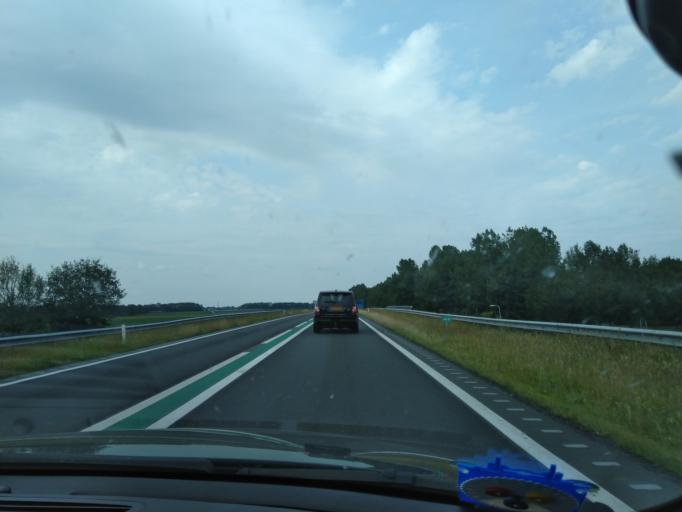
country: NL
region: Drenthe
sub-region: Gemeente Coevorden
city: Dalen
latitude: 52.6967
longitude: 6.7435
